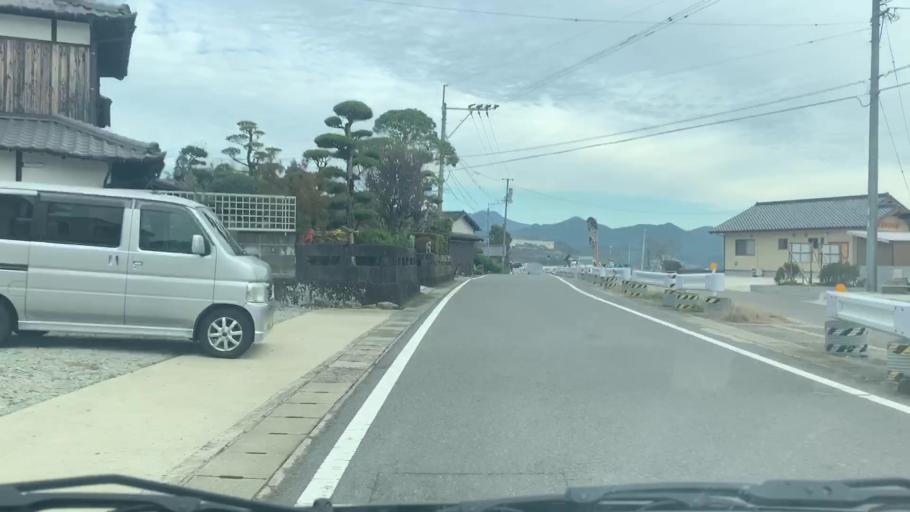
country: JP
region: Saga Prefecture
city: Takeocho-takeo
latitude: 33.2015
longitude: 129.9611
